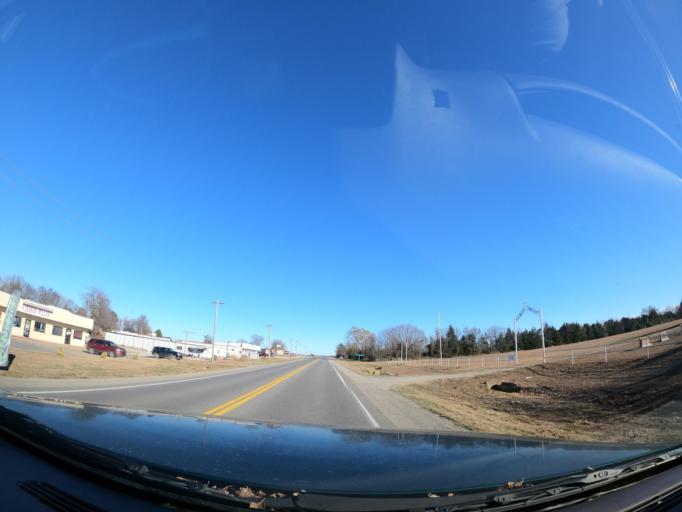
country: US
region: Oklahoma
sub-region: Pittsburg County
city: Longtown
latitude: 35.2392
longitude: -95.5282
